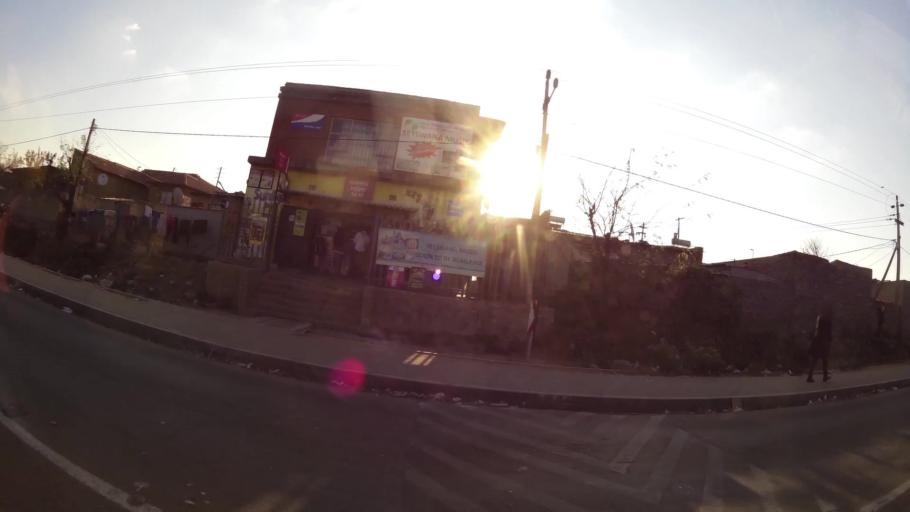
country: ZA
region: Gauteng
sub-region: Ekurhuleni Metropolitan Municipality
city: Tembisa
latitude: -26.0135
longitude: 28.1858
